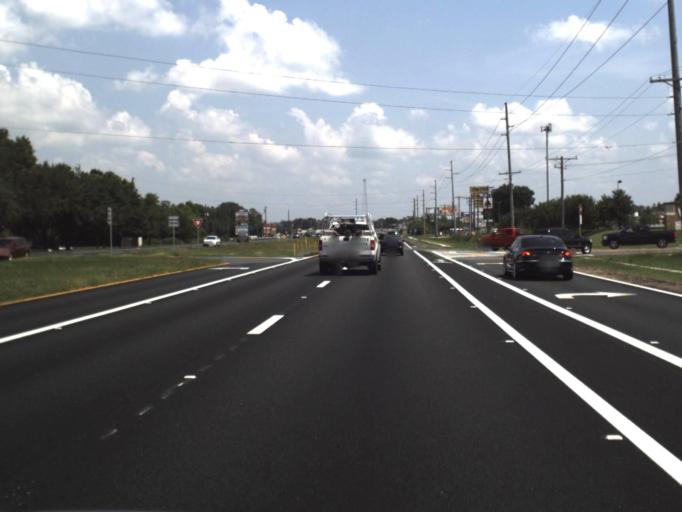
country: US
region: Florida
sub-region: Hillsborough County
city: Lutz
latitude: 28.1792
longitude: -82.4698
